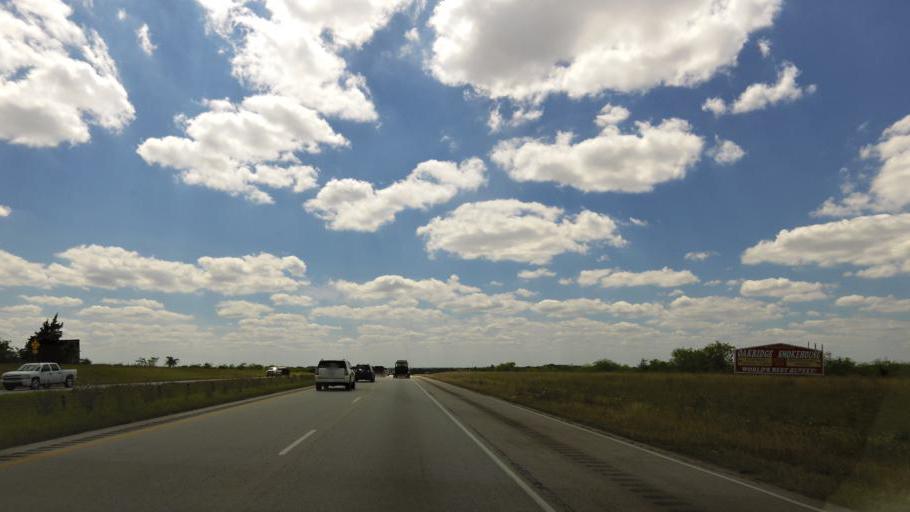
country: US
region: Texas
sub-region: Colorado County
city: Weimar
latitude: 29.6893
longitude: -96.8119
